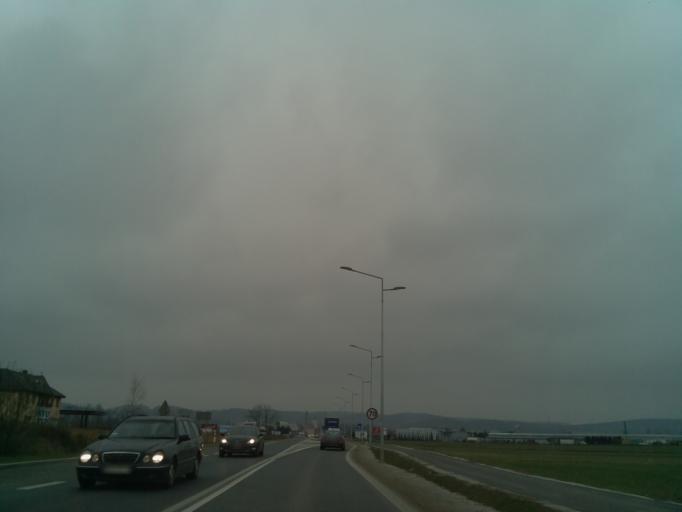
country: PL
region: Lower Silesian Voivodeship
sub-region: Powiat swidnicki
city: Swiebodzice
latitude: 50.8751
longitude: 16.3311
